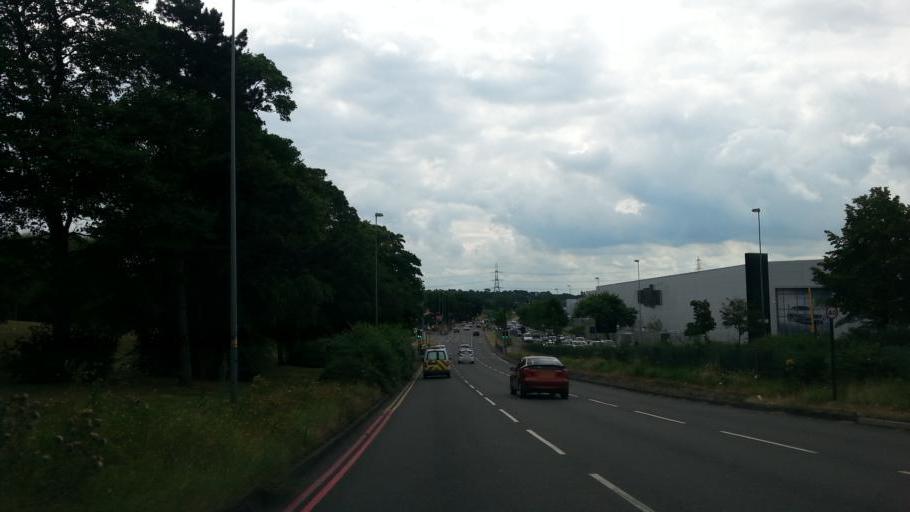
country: GB
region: England
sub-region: City and Borough of Birmingham
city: Sutton Coldfield
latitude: 52.5187
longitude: -1.8001
